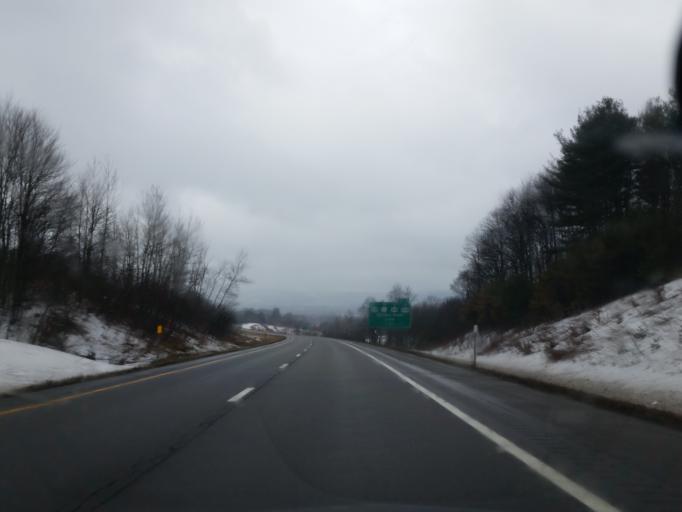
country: US
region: New York
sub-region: Chenango County
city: Lakeview
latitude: 42.3571
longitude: -75.9931
